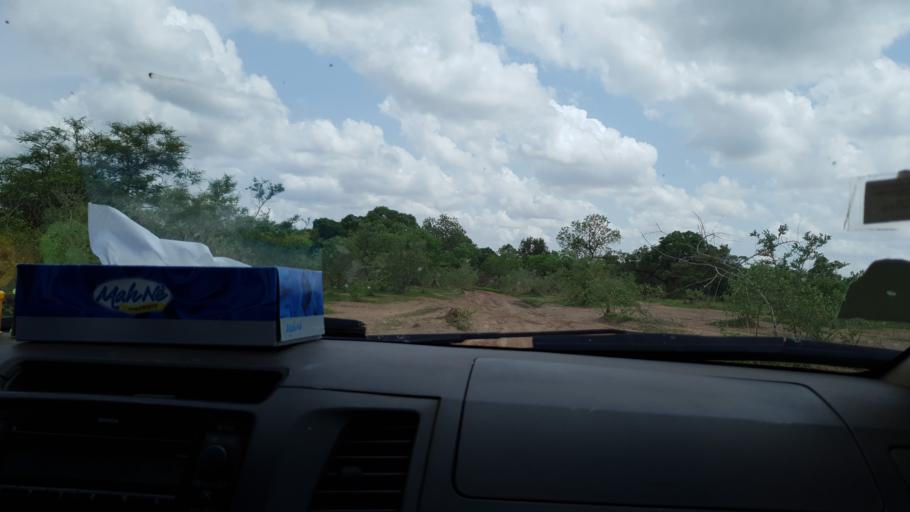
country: ML
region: Segou
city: Baroueli
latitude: 13.3494
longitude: -7.0951
